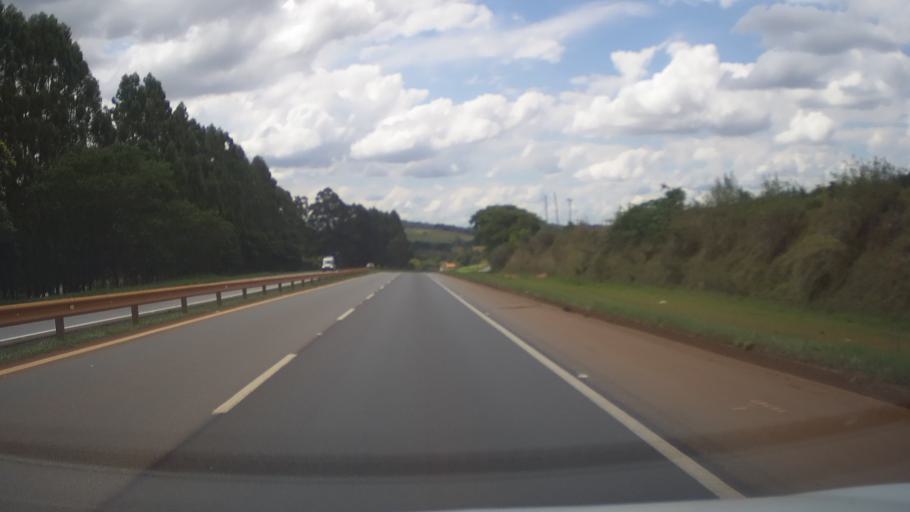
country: BR
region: Minas Gerais
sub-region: Nepomuceno
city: Nepomuceno
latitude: -21.2403
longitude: -45.1354
